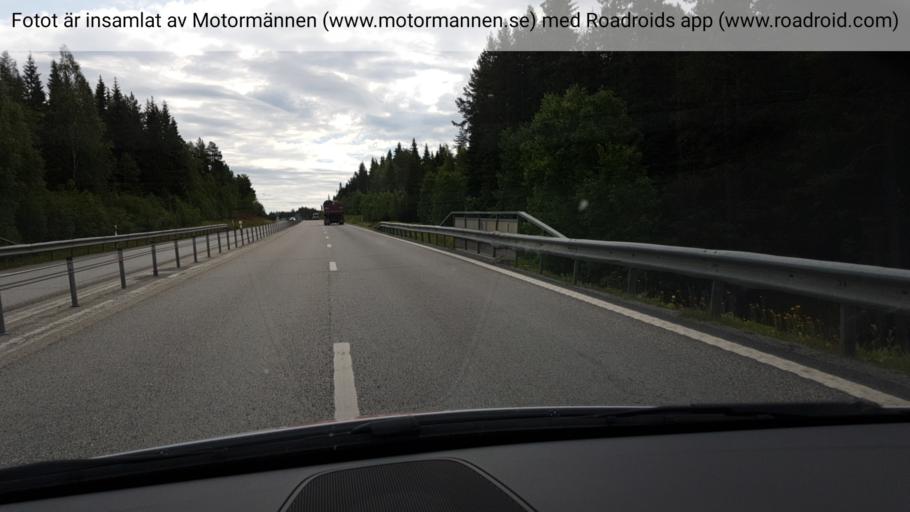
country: SE
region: Jaemtland
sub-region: OEstersunds Kommun
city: Ostersund
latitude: 63.1692
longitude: 14.7116
